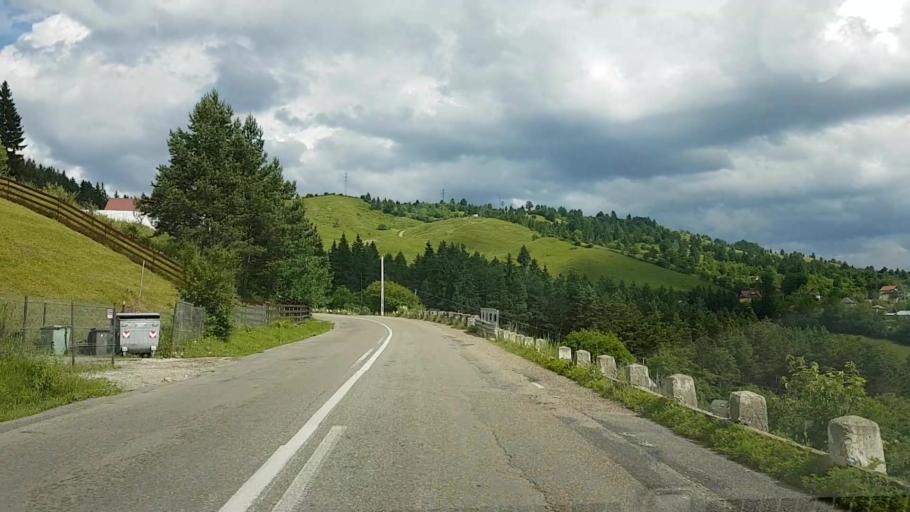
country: RO
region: Neamt
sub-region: Comuna Hangu
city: Hangu
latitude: 47.0064
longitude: 26.0935
